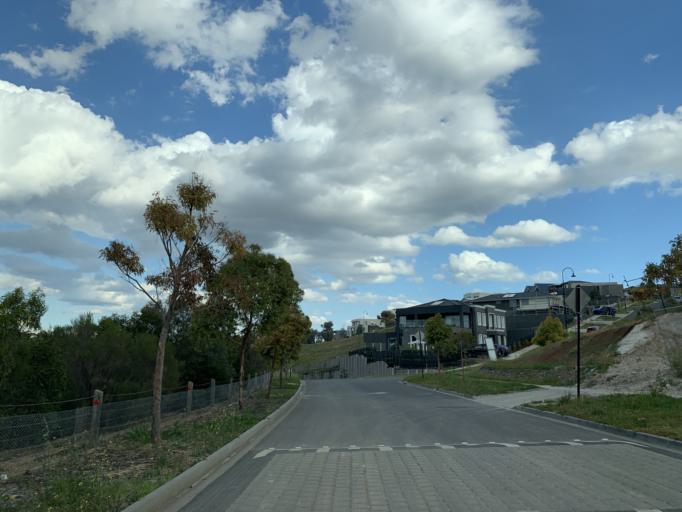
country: AU
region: Victoria
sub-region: Brimbank
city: Albion
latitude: -37.7611
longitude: 144.8482
